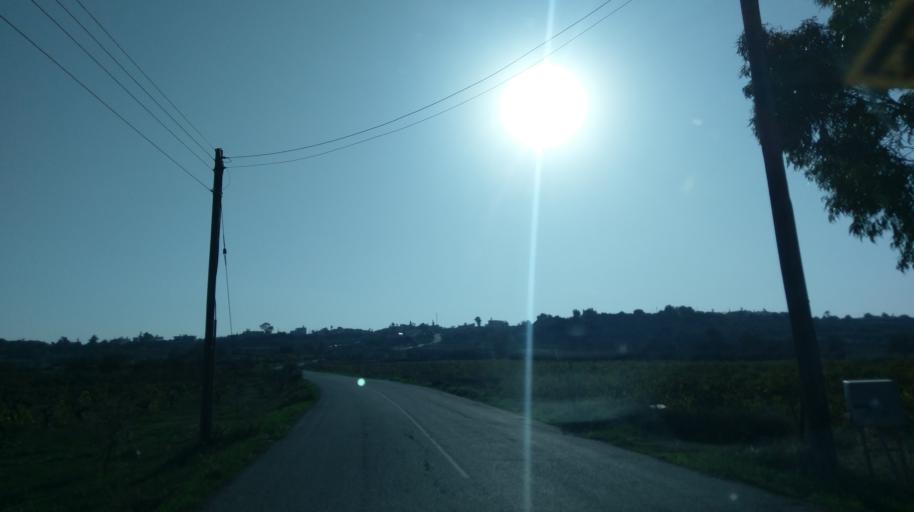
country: CY
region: Ammochostos
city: Leonarisso
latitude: 35.4289
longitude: 34.0777
